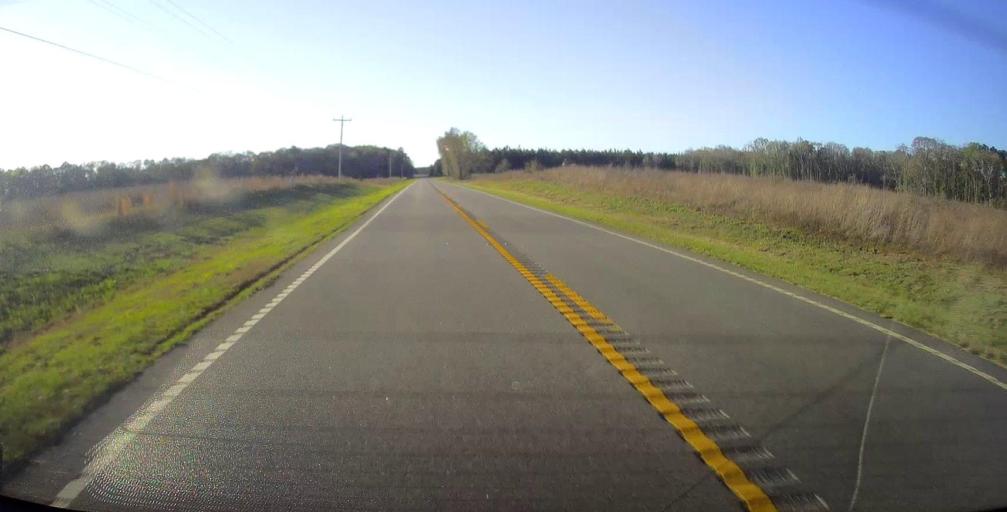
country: US
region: Georgia
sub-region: Pulaski County
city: Hawkinsville
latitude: 32.2575
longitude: -83.4164
